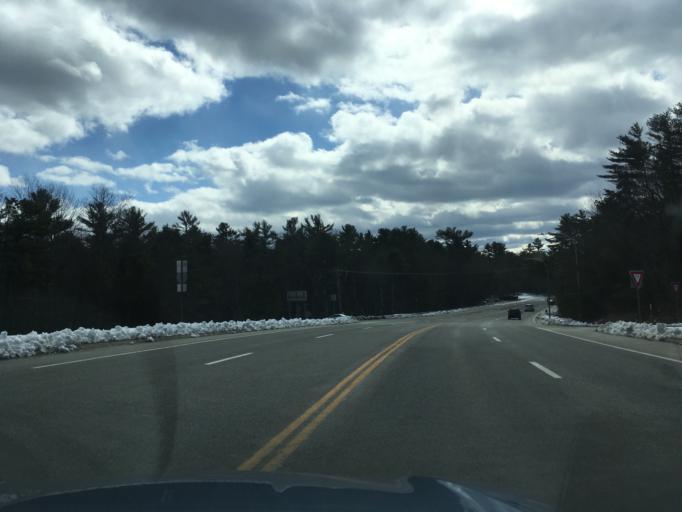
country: US
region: Rhode Island
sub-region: Kent County
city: West Greenwich
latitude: 41.6501
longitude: -71.6063
